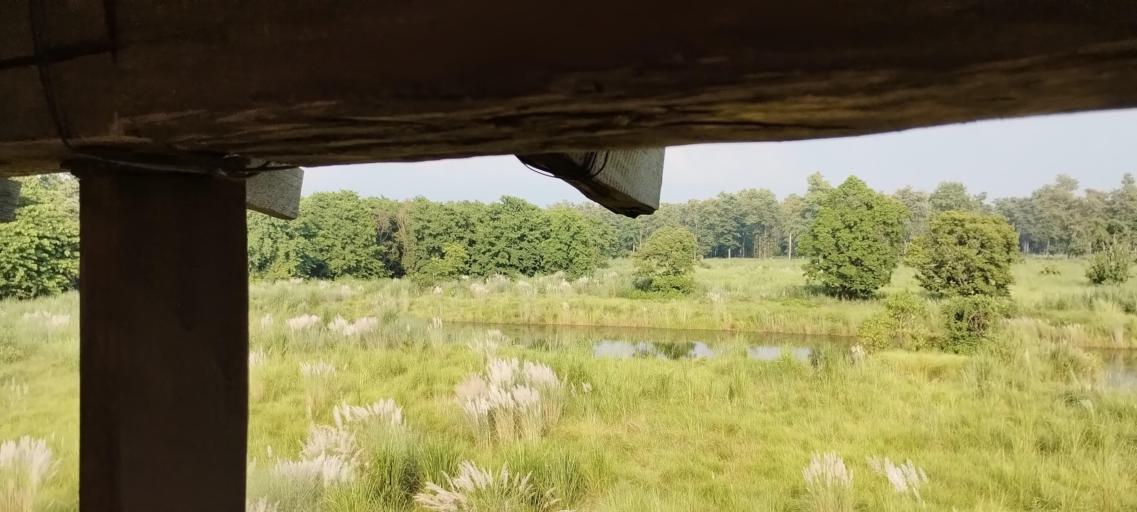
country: NP
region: Far Western
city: Tikapur
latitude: 28.5178
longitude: 81.2887
